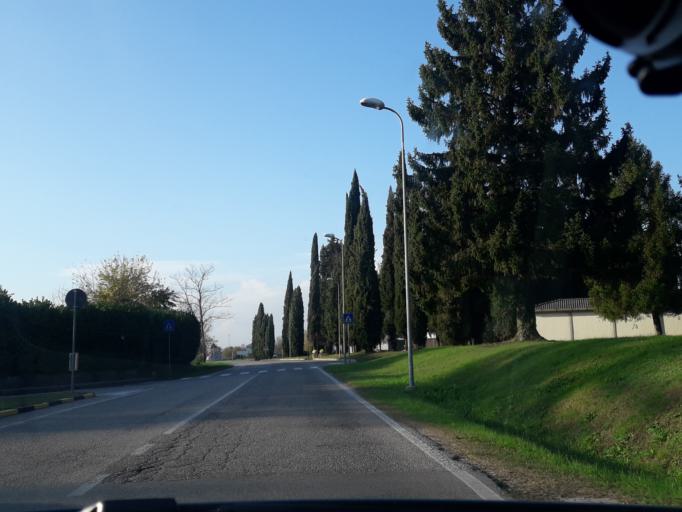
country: IT
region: Friuli Venezia Giulia
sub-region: Provincia di Udine
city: Pradamano
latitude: 46.0344
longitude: 13.2982
